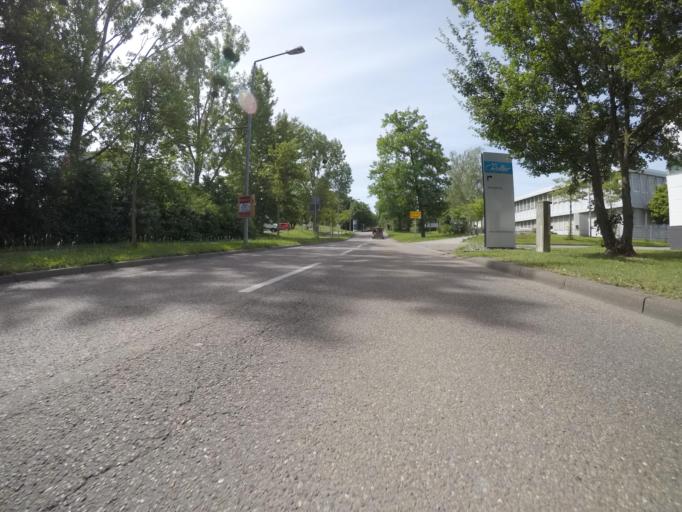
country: DE
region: Baden-Wuerttemberg
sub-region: Regierungsbezirk Stuttgart
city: Gerlingen
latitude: 48.8091
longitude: 9.0870
